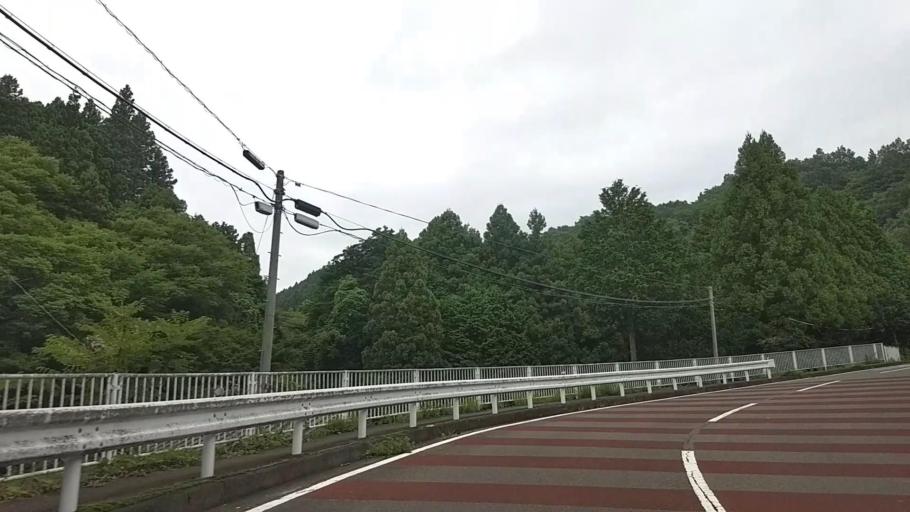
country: JP
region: Shizuoka
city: Gotemba
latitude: 35.3176
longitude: 139.0342
